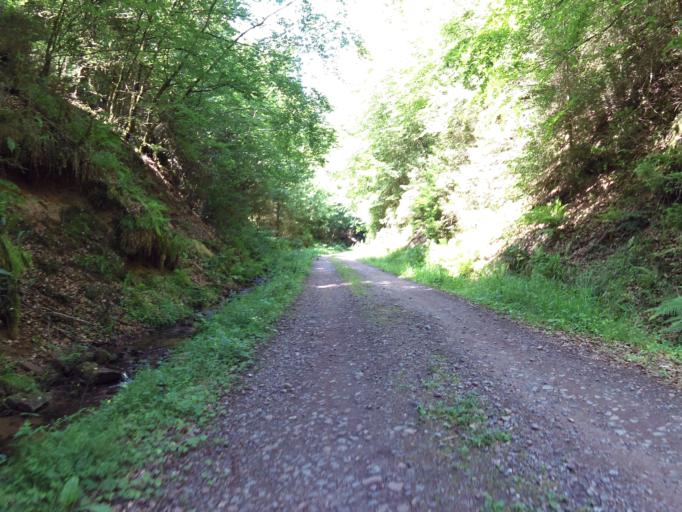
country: DE
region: Rheinland-Pfalz
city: Wilgartswiesen
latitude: 49.2617
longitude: 7.8852
